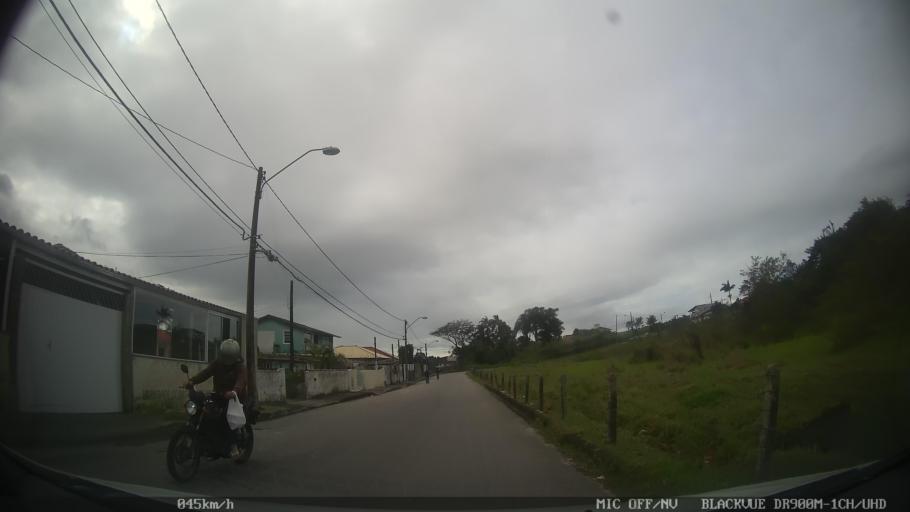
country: BR
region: Santa Catarina
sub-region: Biguacu
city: Biguacu
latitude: -27.5377
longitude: -48.6375
